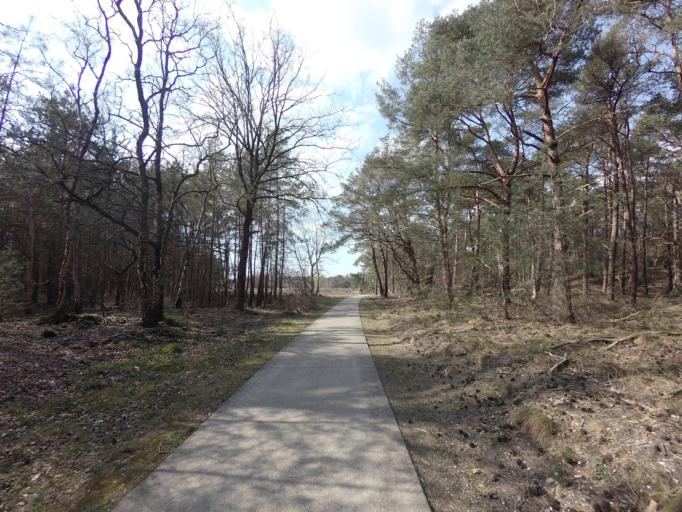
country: NL
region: Gelderland
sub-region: Gemeente Nunspeet
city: Nunspeet
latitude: 52.3484
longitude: 5.7642
